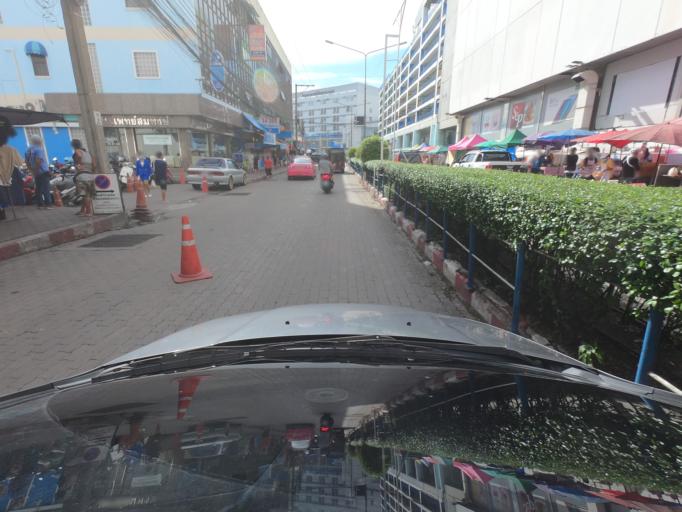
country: TH
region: Bangkok
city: Bang Na
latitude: 13.6499
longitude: 100.5956
